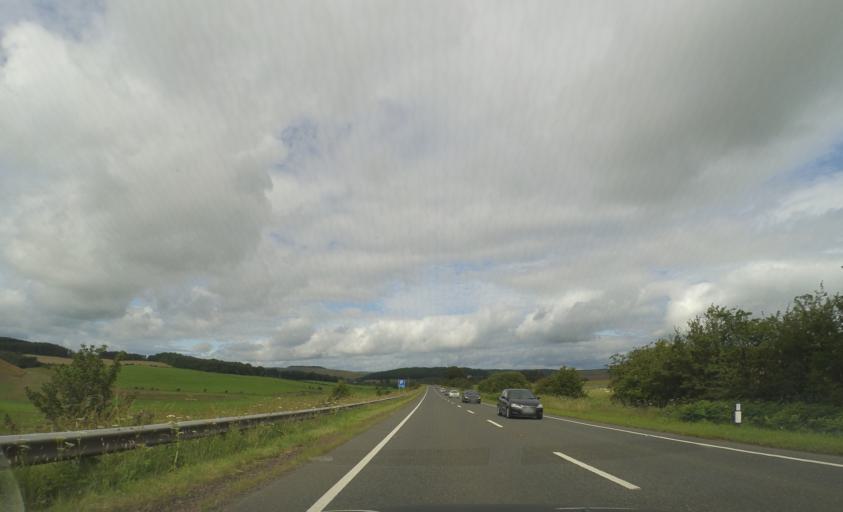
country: GB
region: Scotland
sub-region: The Scottish Borders
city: Selkirk
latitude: 55.4814
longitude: -2.8232
